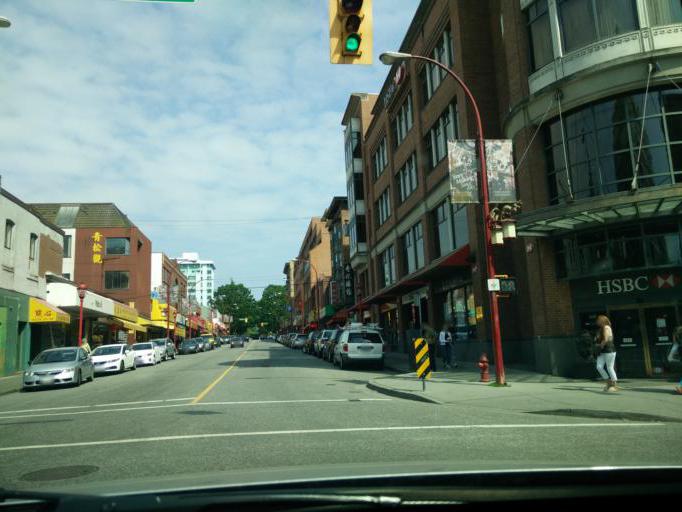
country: CA
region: British Columbia
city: West End
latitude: 49.2795
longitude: -123.0998
